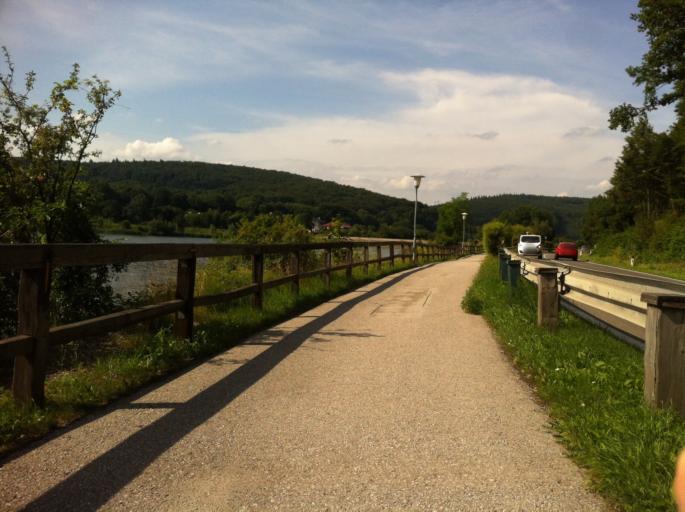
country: AT
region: Lower Austria
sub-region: Politischer Bezirk Wien-Umgebung
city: Wolfsgraben
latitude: 48.1792
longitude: 16.1226
